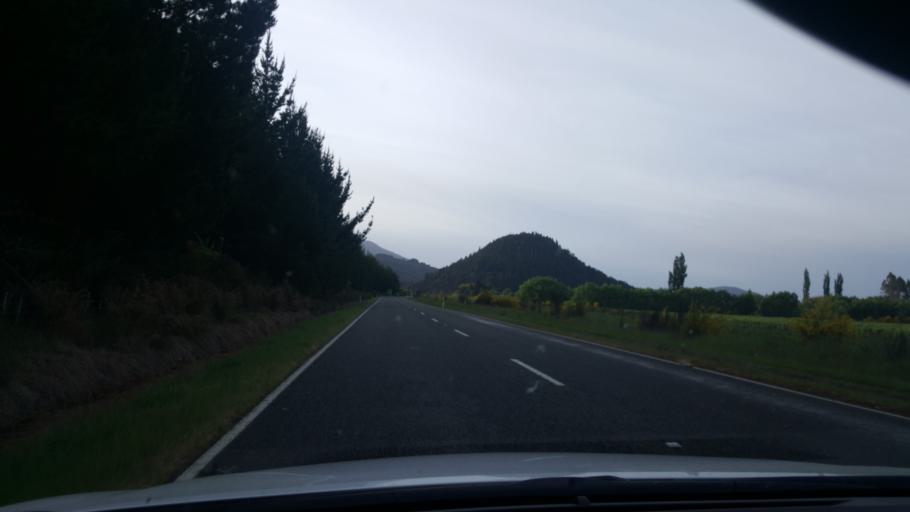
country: NZ
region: Waikato
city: Turangi
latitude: -38.9853
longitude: 175.7849
